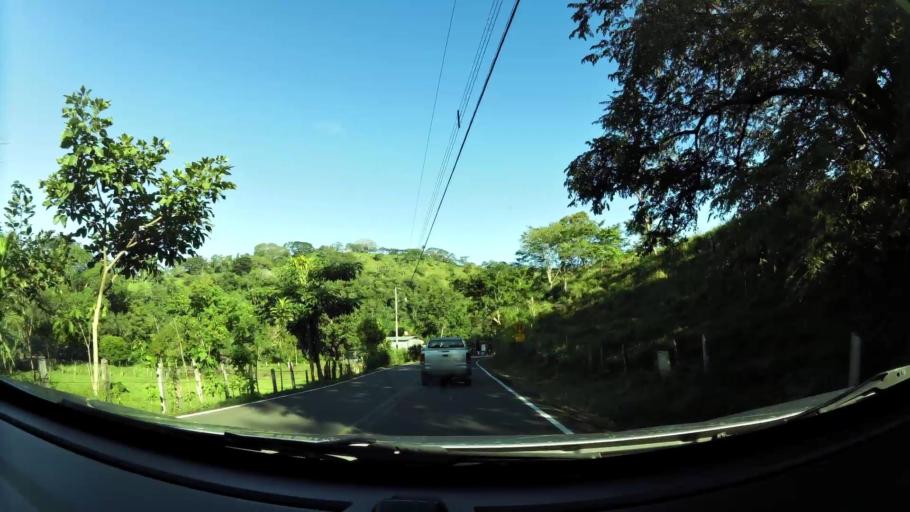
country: CR
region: Guanacaste
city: Juntas
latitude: 10.2147
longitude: -84.8501
